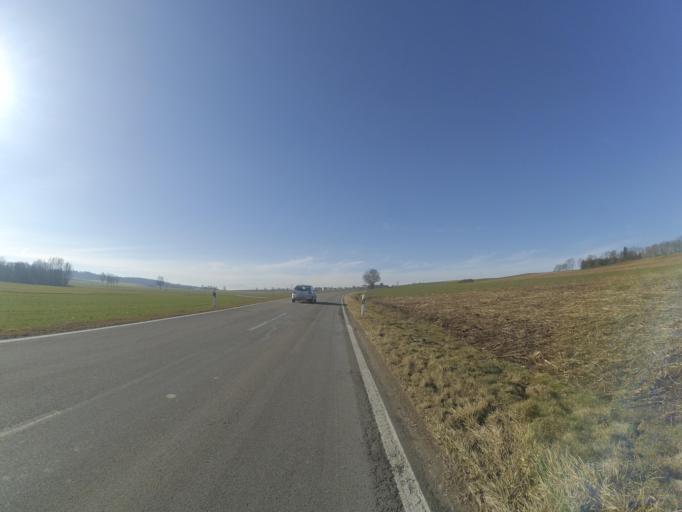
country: DE
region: Baden-Wuerttemberg
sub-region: Tuebingen Region
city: Aulendorf
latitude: 47.9270
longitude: 9.6365
